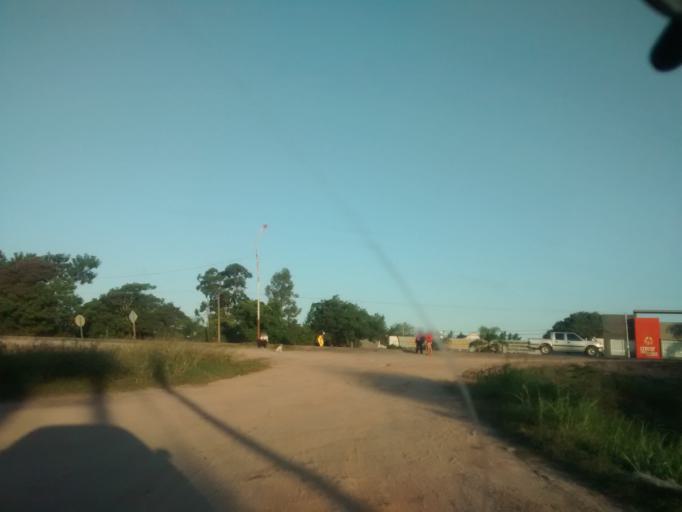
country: AR
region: Chaco
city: Fontana
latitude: -27.4192
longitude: -59.0062
